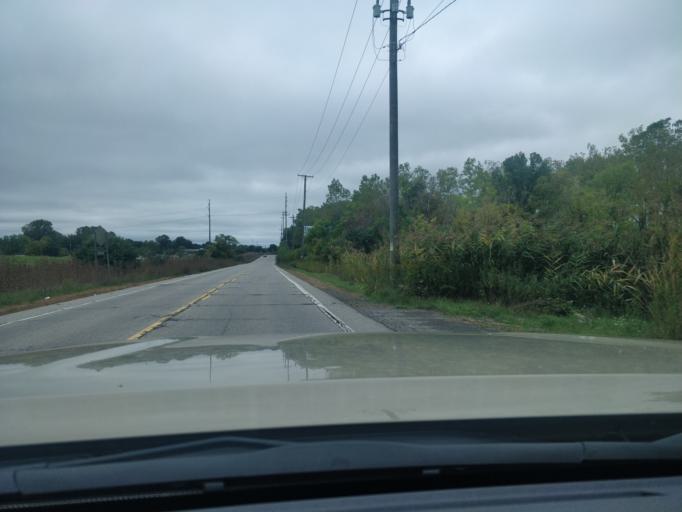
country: US
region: Michigan
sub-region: Wayne County
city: Romulus
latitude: 42.2210
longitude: -83.4292
